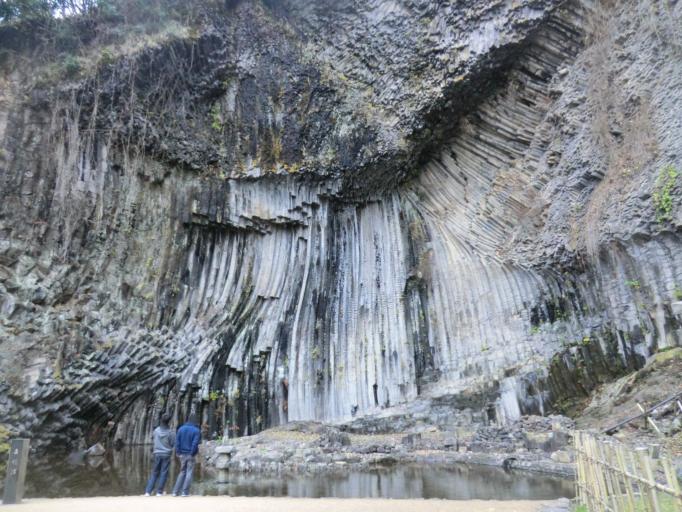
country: JP
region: Hyogo
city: Toyooka
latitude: 35.5877
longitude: 134.8050
